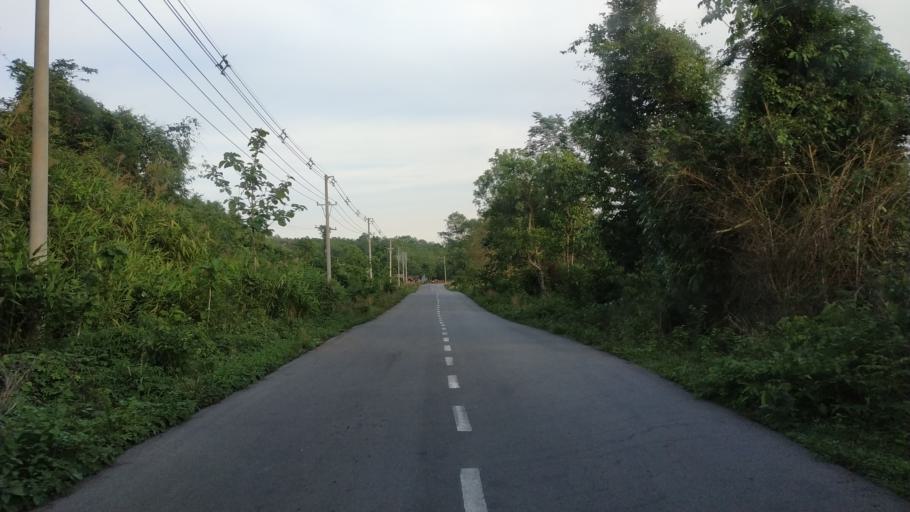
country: MM
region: Mon
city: Kyaikto
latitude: 17.4150
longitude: 97.0717
